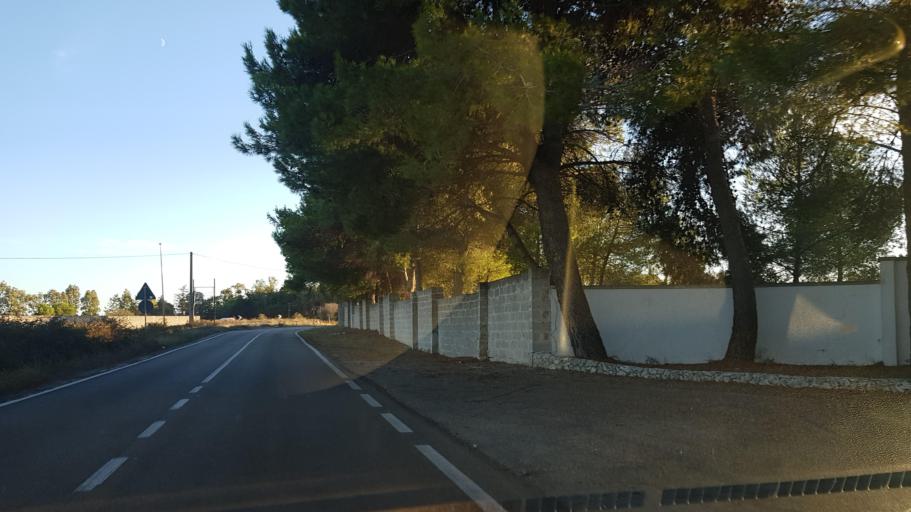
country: IT
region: Apulia
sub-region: Provincia di Lecce
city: Giorgilorio
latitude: 40.4097
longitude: 18.2010
